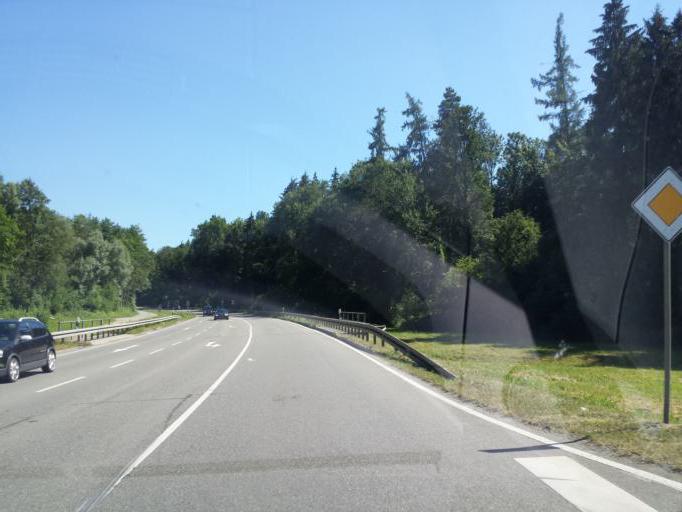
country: DE
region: Baden-Wuerttemberg
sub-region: Freiburg Region
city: Stockach
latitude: 47.8368
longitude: 8.9888
